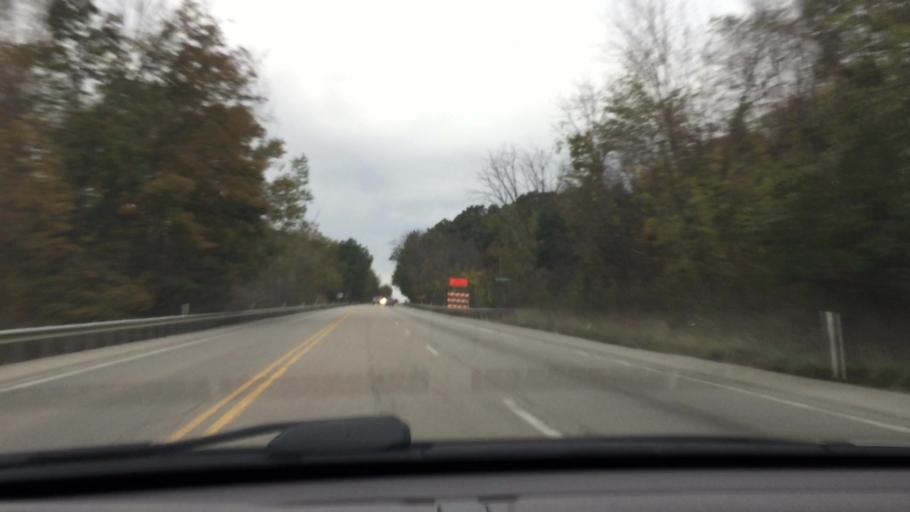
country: US
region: Pennsylvania
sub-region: Lawrence County
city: Oakwood
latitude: 41.0397
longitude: -80.4153
